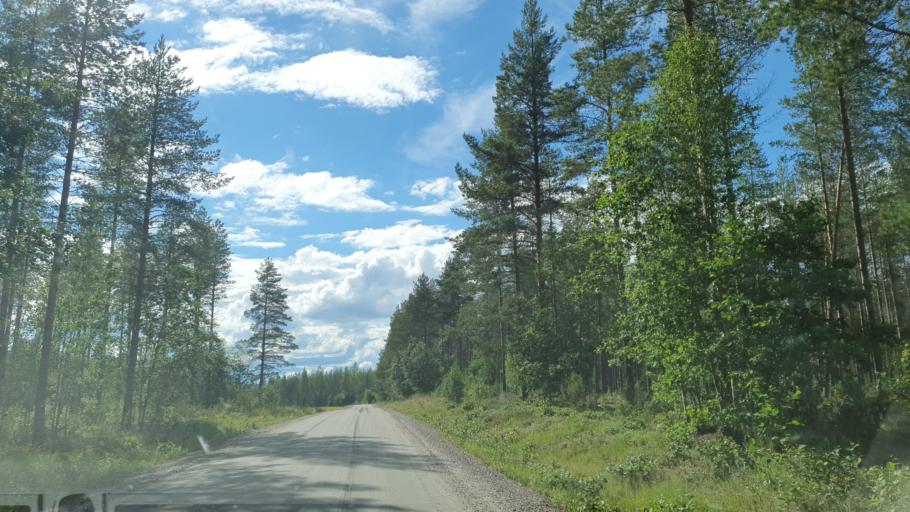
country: FI
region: Kainuu
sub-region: Kehys-Kainuu
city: Kuhmo
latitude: 64.1398
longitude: 29.6900
